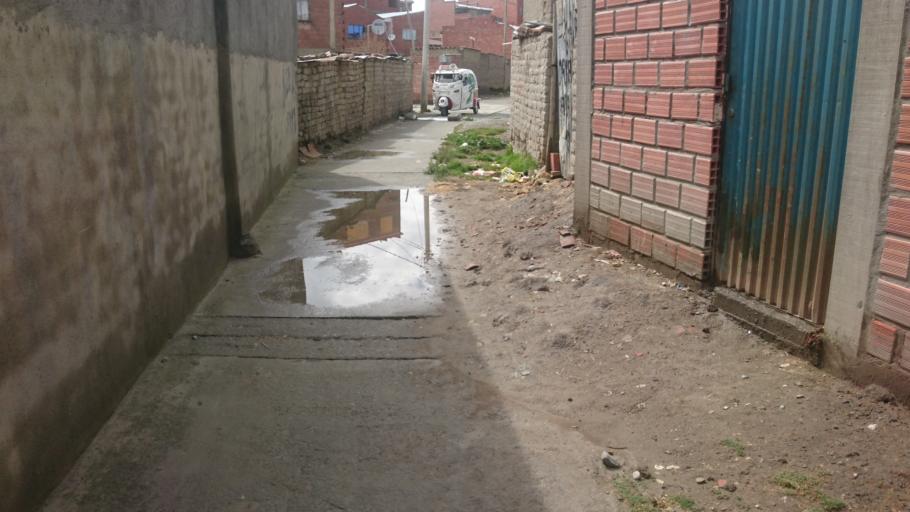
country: BO
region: La Paz
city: Achacachi
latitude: -16.0464
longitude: -68.6842
